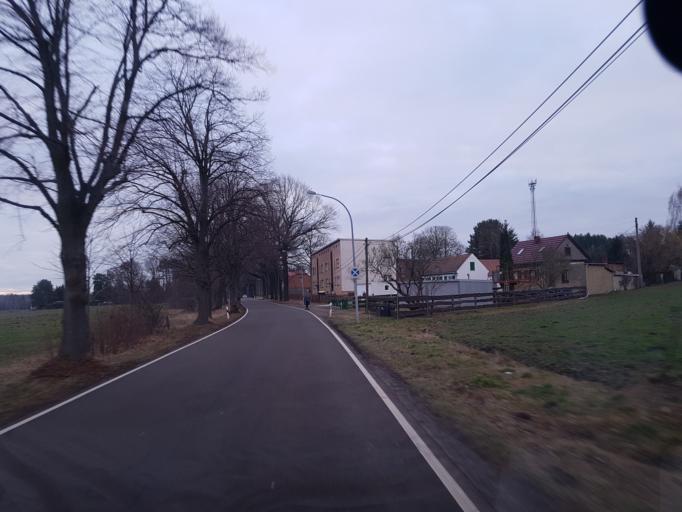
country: DE
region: Brandenburg
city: Schipkau
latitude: 51.5385
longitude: 13.8992
